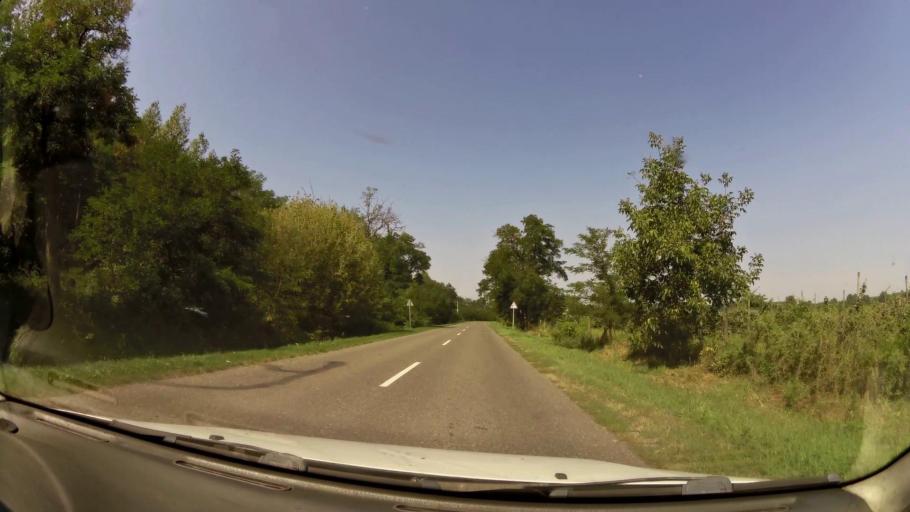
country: HU
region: Pest
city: Ujszilvas
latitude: 47.2744
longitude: 19.8845
